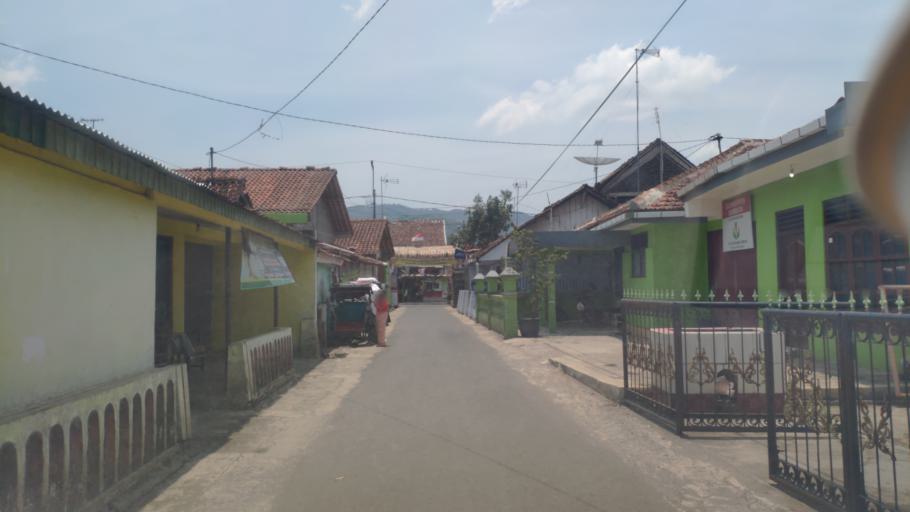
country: ID
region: Central Java
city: Wonosobo
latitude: -7.3917
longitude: 109.7084
